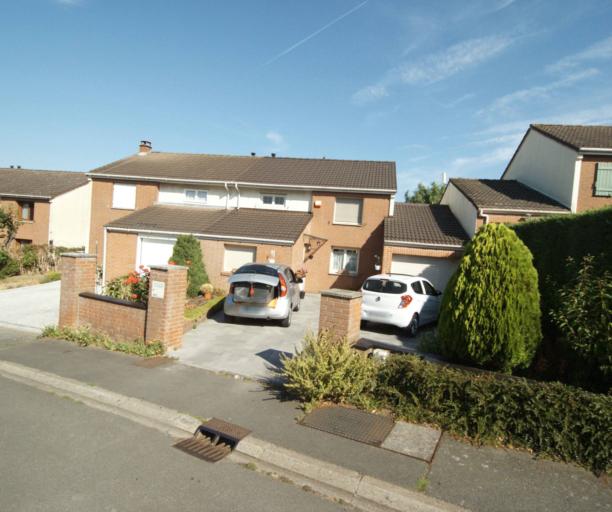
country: FR
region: Nord-Pas-de-Calais
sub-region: Departement du Nord
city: Halluin
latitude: 50.7744
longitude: 3.1419
